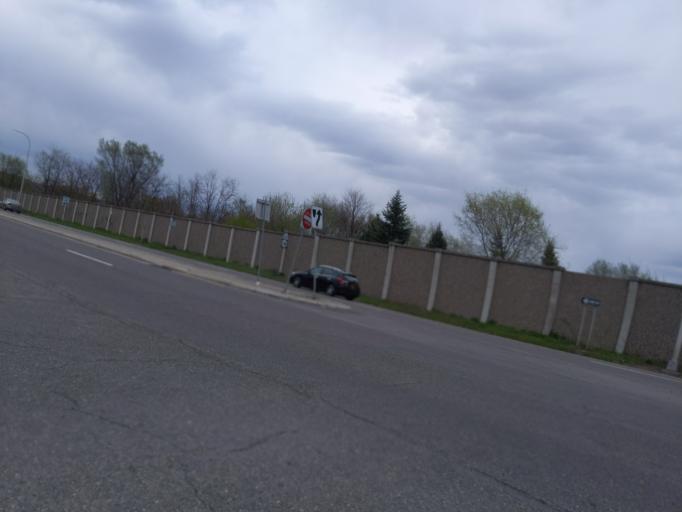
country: US
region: New York
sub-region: Chemung County
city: Elmira
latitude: 42.0706
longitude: -76.8022
